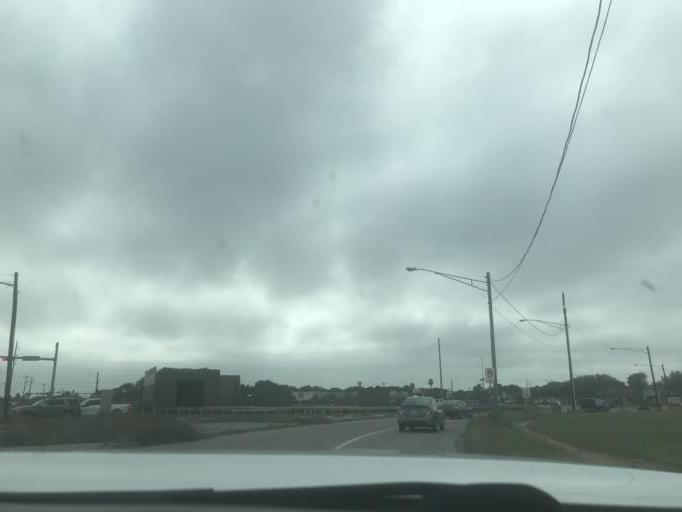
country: US
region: Texas
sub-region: Nueces County
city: Corpus Christi
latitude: 27.6868
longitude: -97.3638
